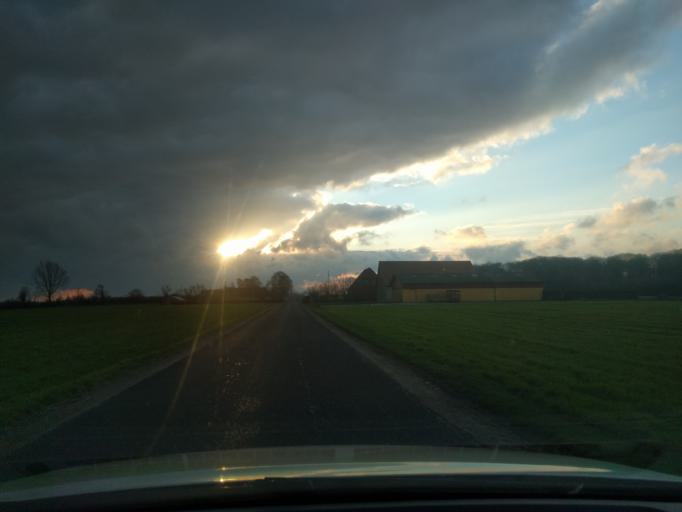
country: DK
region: South Denmark
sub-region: Nyborg Kommune
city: Ullerslev
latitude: 55.3797
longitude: 10.6433
